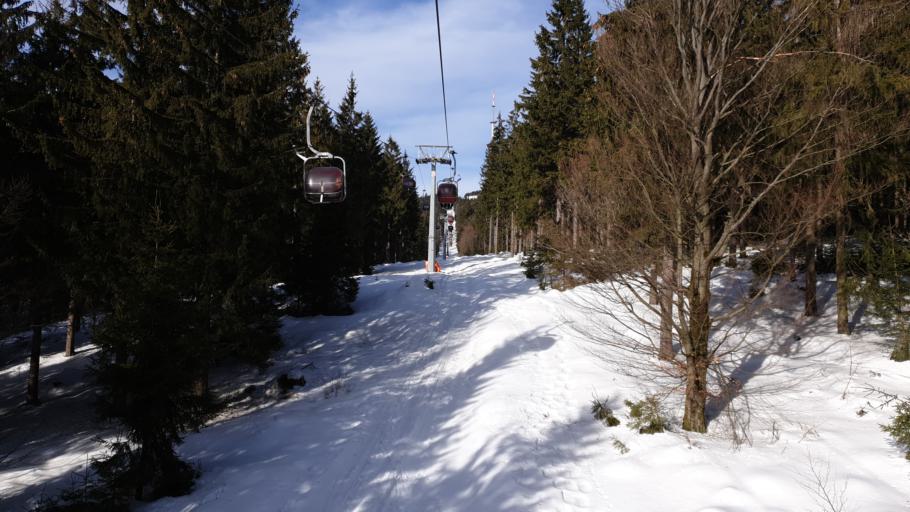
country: DE
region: Bavaria
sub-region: Upper Franconia
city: Bischofsgrun
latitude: 50.0189
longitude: 11.8084
